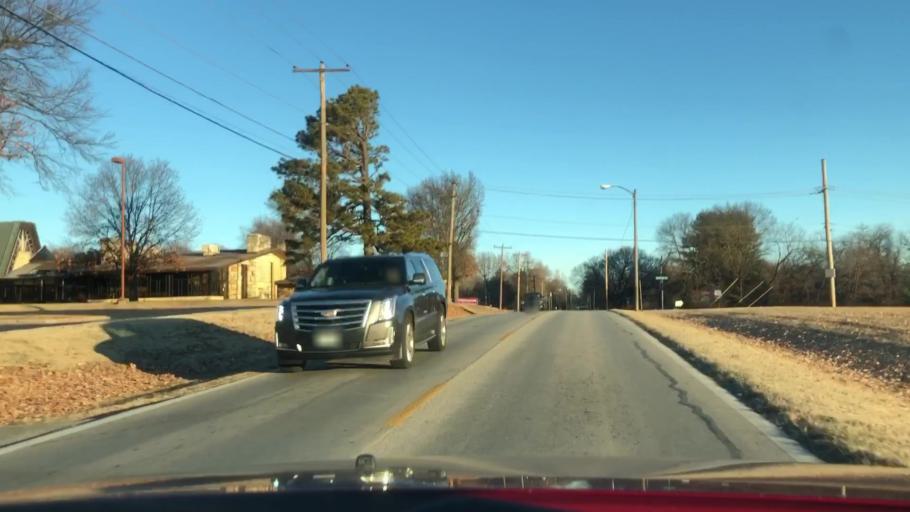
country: US
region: Missouri
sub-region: Greene County
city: Springfield
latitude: 37.1688
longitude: -93.2466
